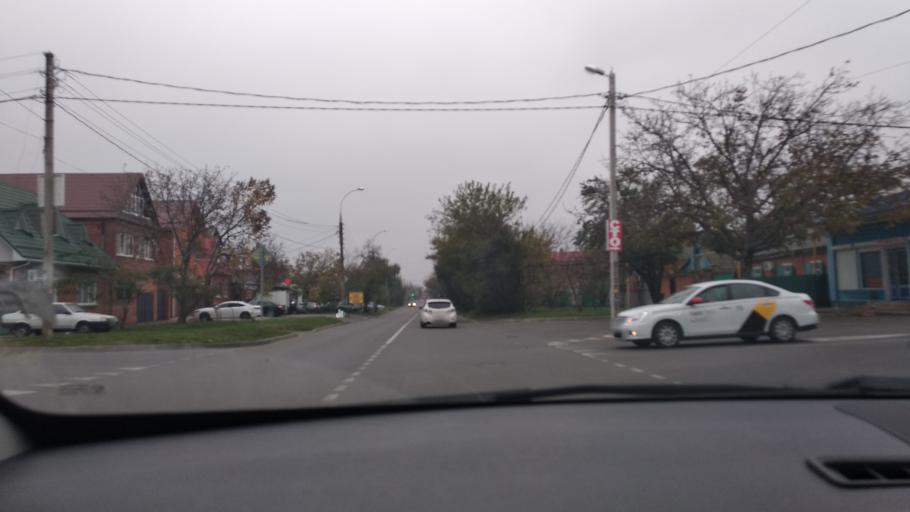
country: RU
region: Krasnodarskiy
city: Krasnodar
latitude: 45.0181
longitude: 39.0104
